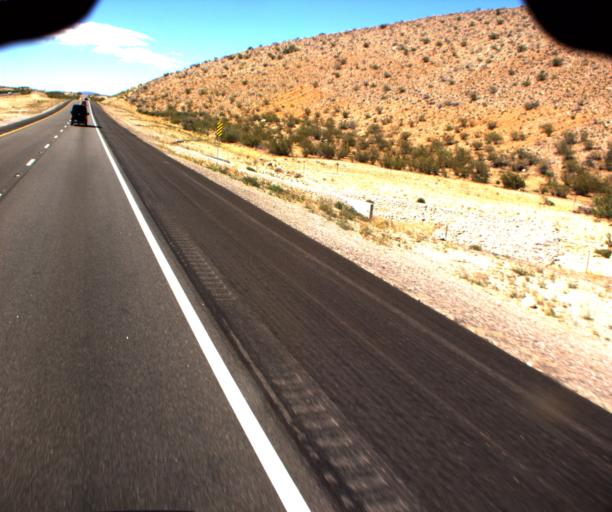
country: US
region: Arizona
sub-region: Mohave County
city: Kingman
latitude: 35.0159
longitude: -113.6640
